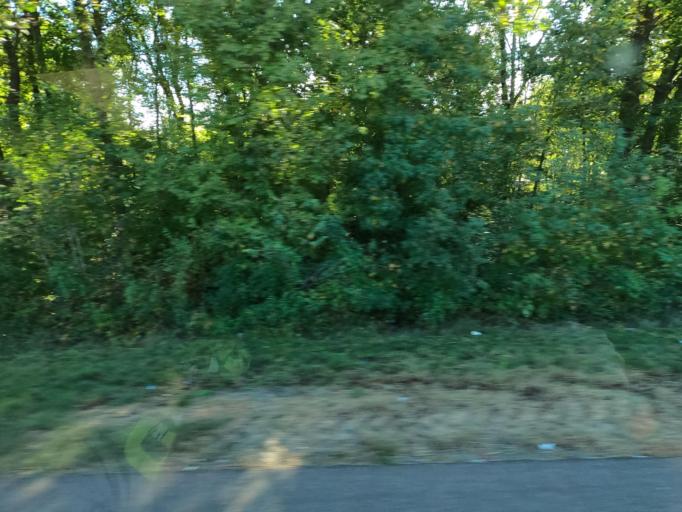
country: US
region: Tennessee
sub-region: Tipton County
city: Munford
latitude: 35.4297
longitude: -89.8086
